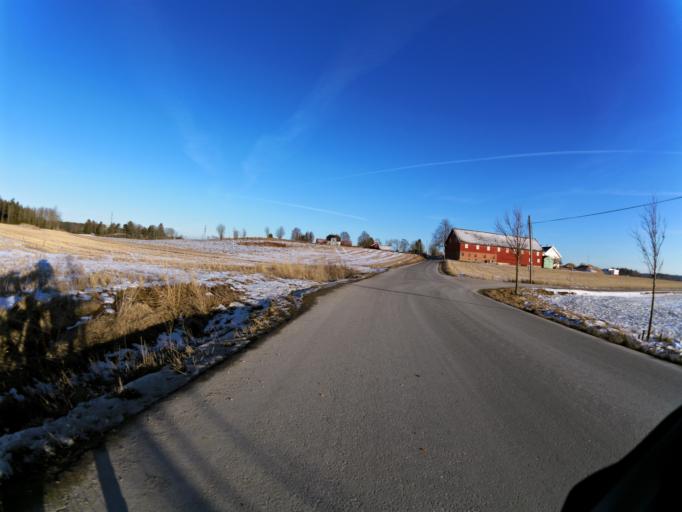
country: NO
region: Ostfold
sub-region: Fredrikstad
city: Lervik
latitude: 59.2529
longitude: 10.8100
